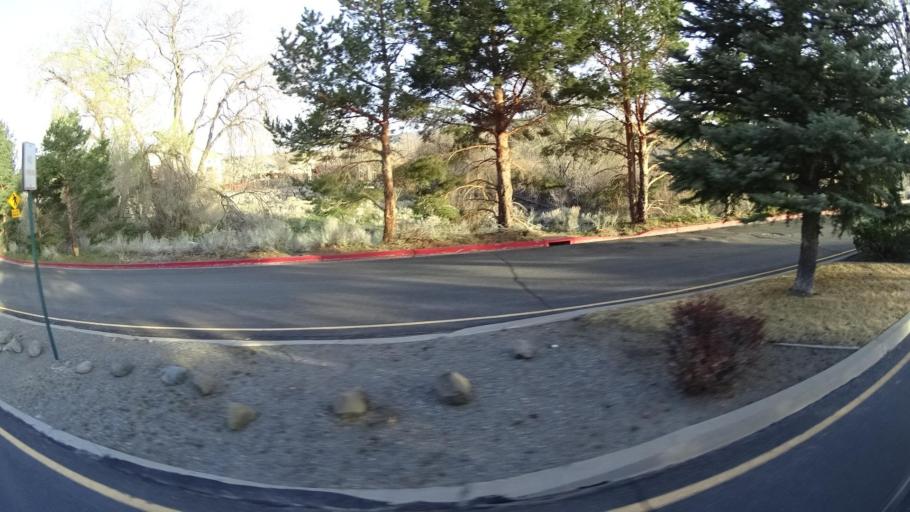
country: US
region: Nevada
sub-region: Washoe County
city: Mogul
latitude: 39.5056
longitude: -119.9028
